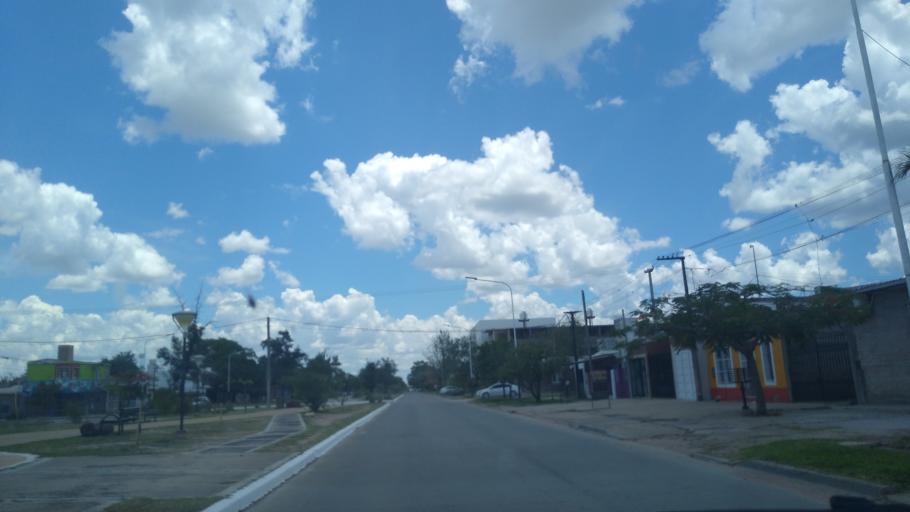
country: AR
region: Chaco
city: Presidencia Roque Saenz Pena
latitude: -26.7783
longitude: -60.4318
